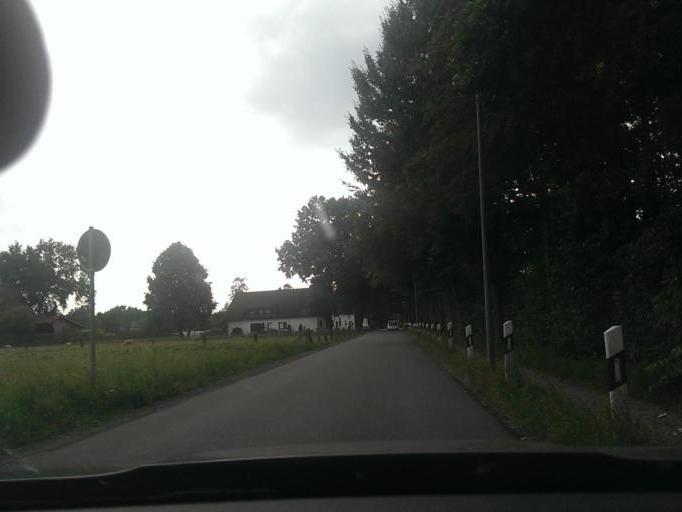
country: DE
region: North Rhine-Westphalia
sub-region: Regierungsbezirk Detmold
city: Delbruck
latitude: 51.7552
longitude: 8.5584
